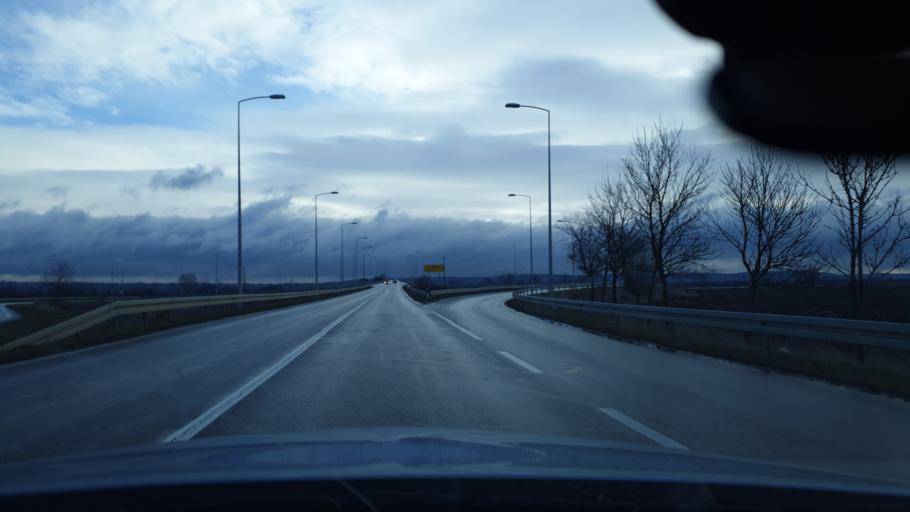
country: RS
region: Central Serbia
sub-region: Branicevski Okrug
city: Pozarevac
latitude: 44.6003
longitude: 21.1466
